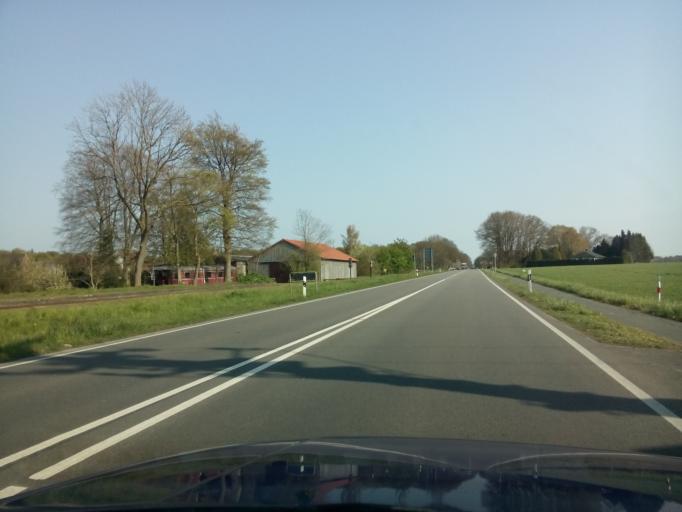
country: DE
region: Lower Saxony
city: Bruchhausen-Vilsen
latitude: 52.8014
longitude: 8.9746
